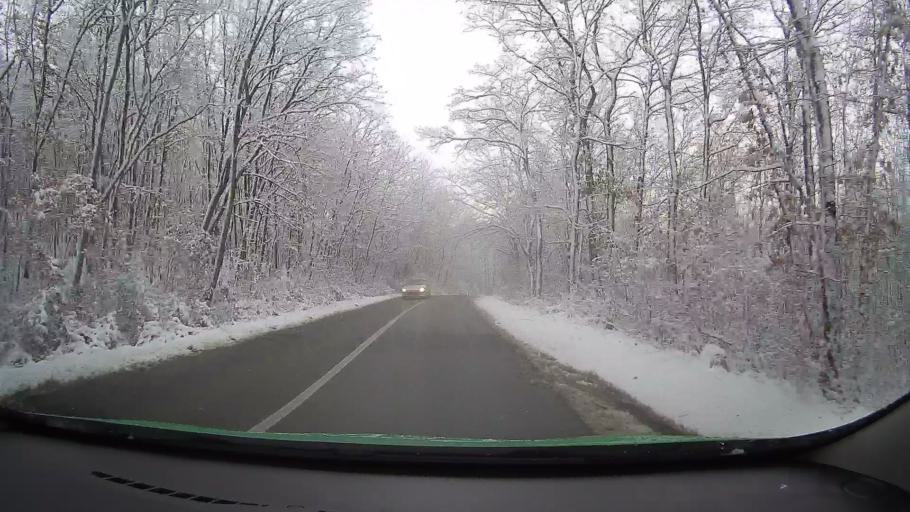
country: RO
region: Hunedoara
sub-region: Oras Hateg
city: Hateg
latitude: 45.6390
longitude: 22.9167
